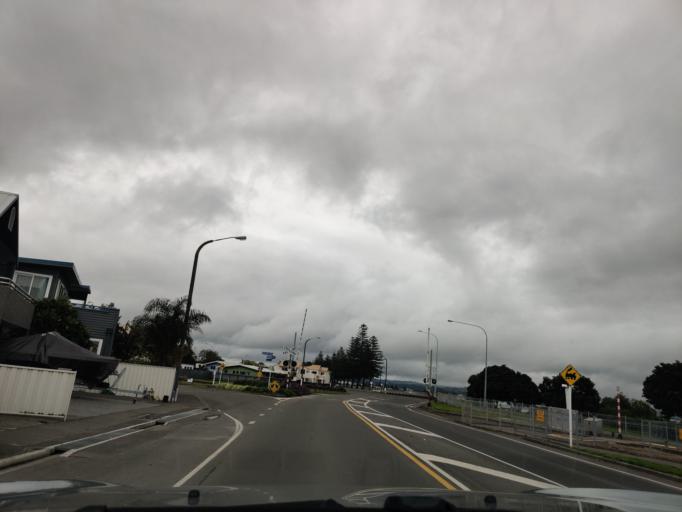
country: NZ
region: Hawke's Bay
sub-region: Napier City
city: Napier
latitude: -39.4781
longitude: 176.9096
